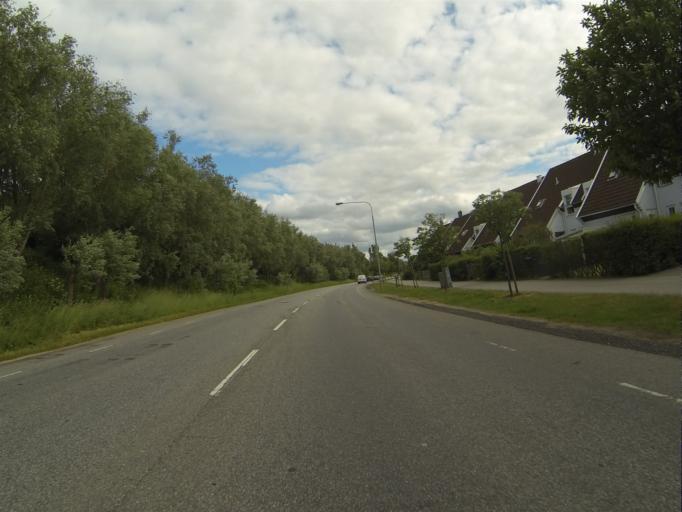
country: SE
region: Skane
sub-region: Burlovs Kommun
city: Arloev
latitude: 55.6164
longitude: 13.0617
